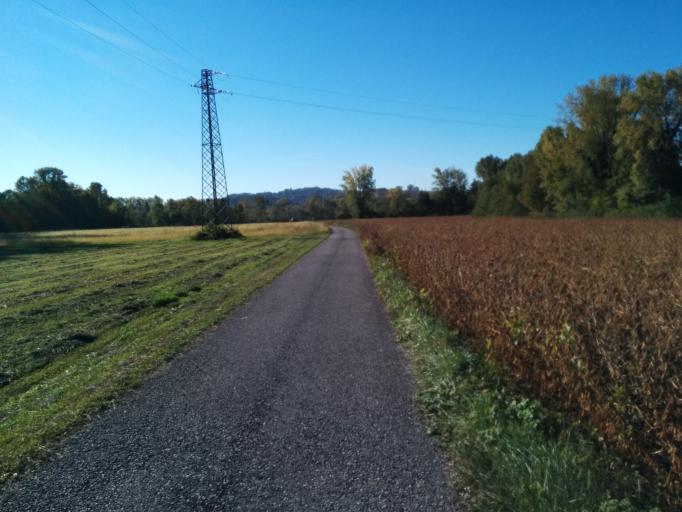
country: IT
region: Friuli Venezia Giulia
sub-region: Provincia di Udine
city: Gemona
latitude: 46.2457
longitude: 13.1237
